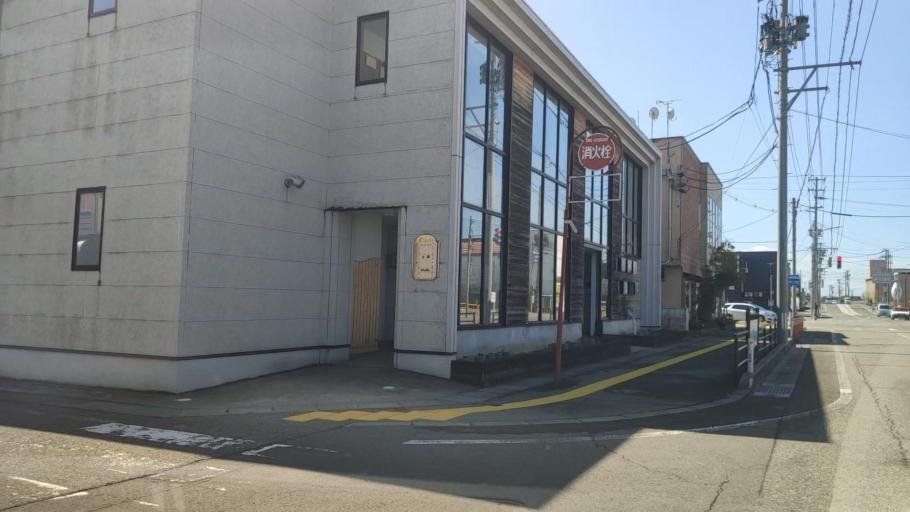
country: JP
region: Akita
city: Omagari
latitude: 39.4629
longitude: 140.4763
